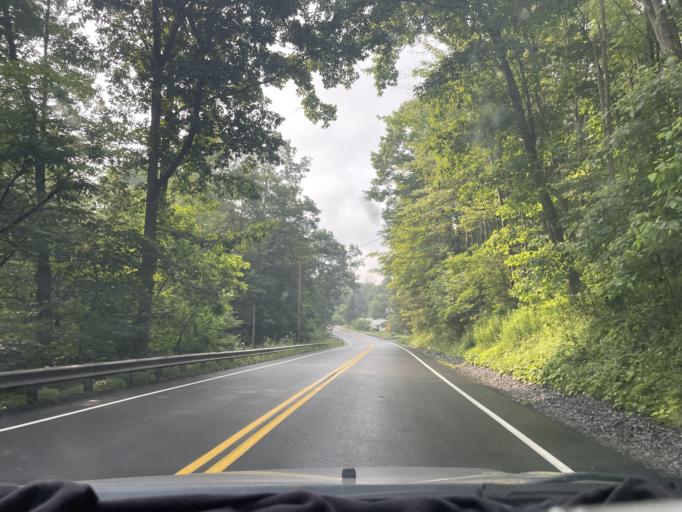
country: US
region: Maryland
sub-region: Garrett County
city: Mountain Lake Park
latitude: 39.3038
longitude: -79.3977
